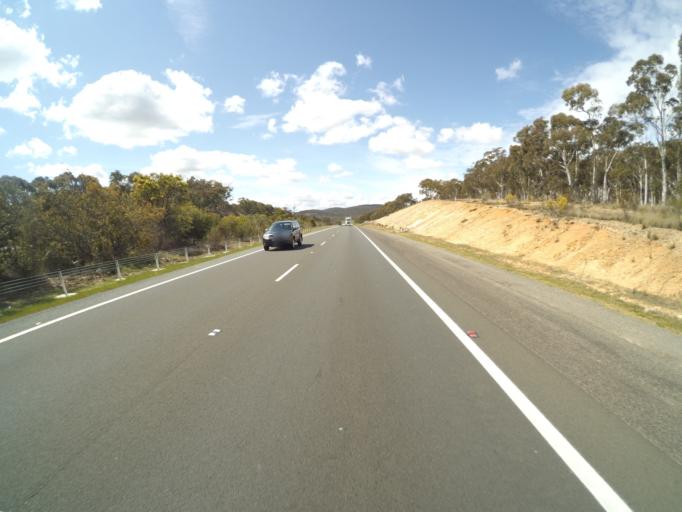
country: AU
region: New South Wales
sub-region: Goulburn Mulwaree
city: Goulburn
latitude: -34.7428
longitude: 149.9021
